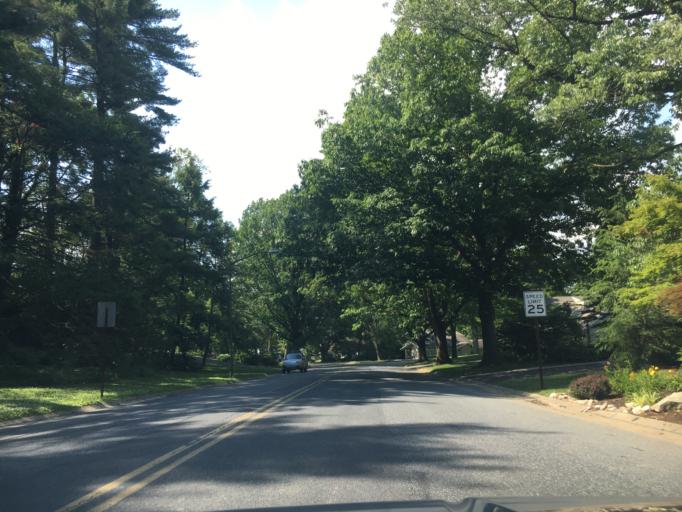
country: US
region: Pennsylvania
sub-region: Berks County
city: Wyomissing
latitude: 40.3207
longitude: -75.9623
